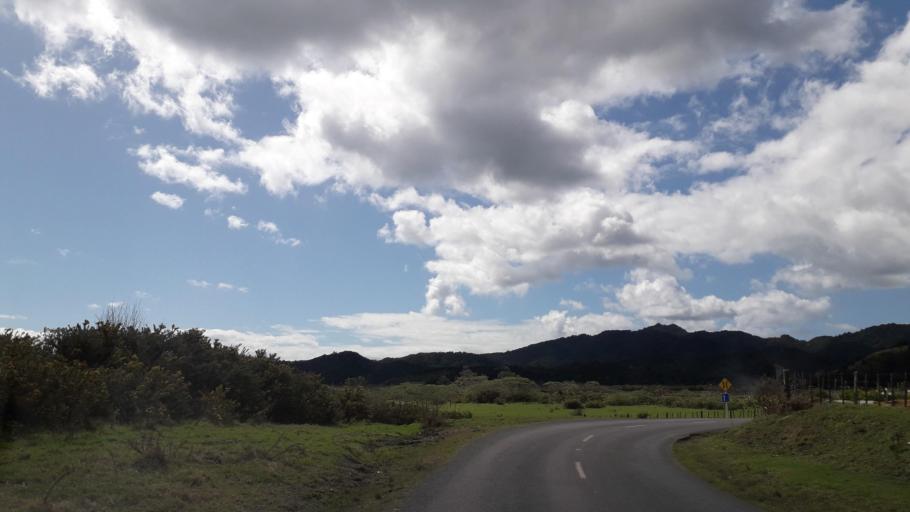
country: NZ
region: Northland
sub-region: Far North District
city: Paihia
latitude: -35.3406
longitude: 174.2253
